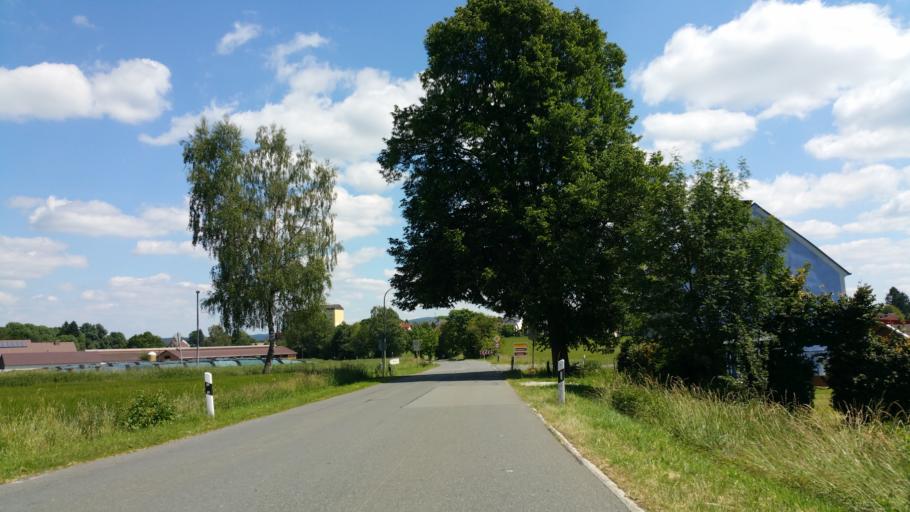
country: DE
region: Bavaria
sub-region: Upper Franconia
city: Schwarzenbach an der Saale
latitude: 50.2219
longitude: 11.9195
